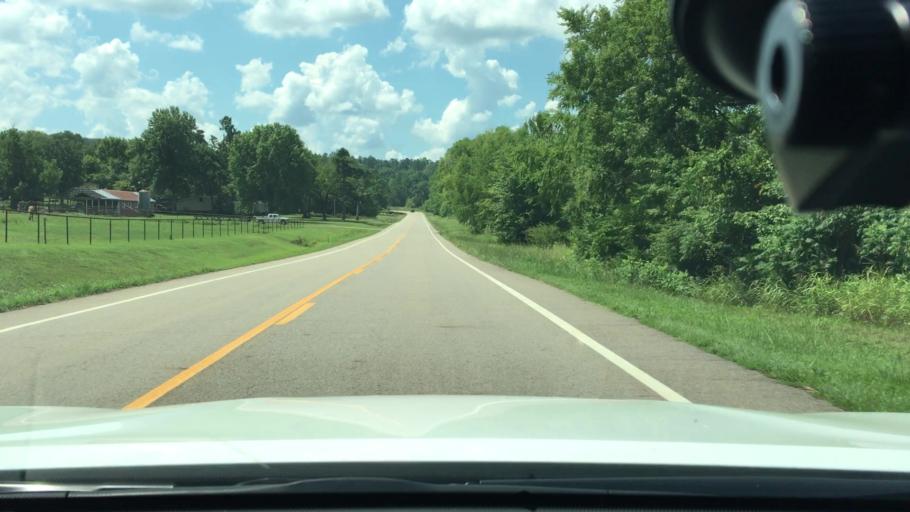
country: US
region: Arkansas
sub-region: Logan County
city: Paris
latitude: 35.2623
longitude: -93.6832
